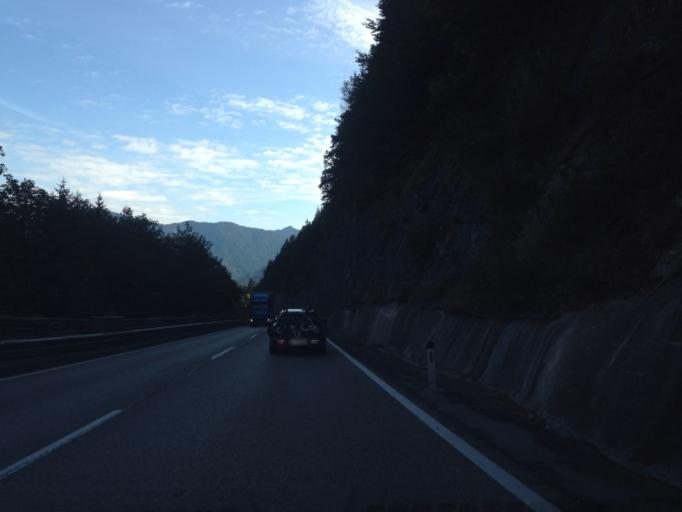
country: AT
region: Tyrol
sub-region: Politischer Bezirk Reutte
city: Reutte
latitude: 47.4642
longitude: 10.7204
